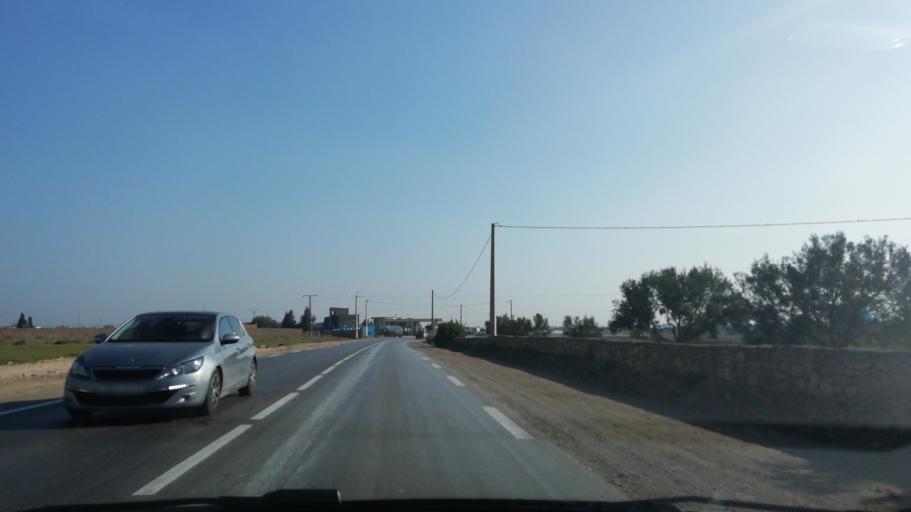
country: DZ
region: Mostaganem
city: Mostaganem
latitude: 35.7423
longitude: -0.0234
